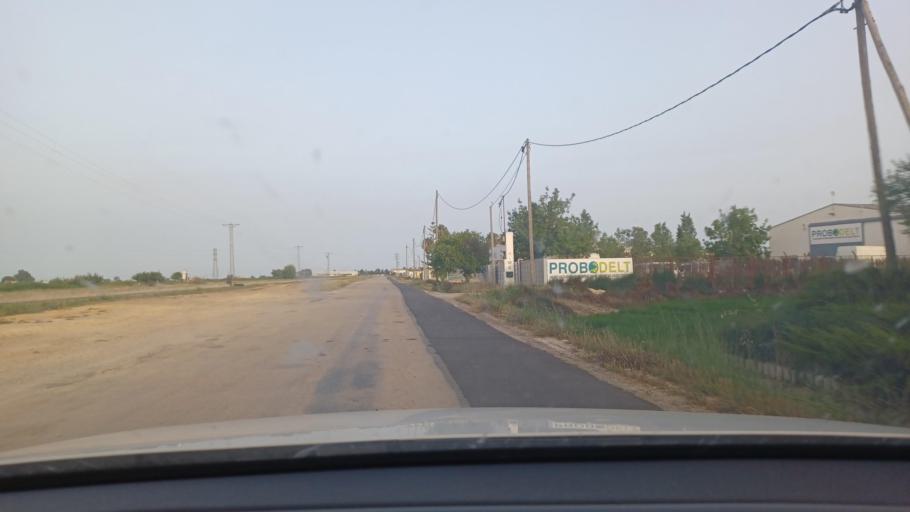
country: ES
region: Catalonia
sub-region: Provincia de Tarragona
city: Amposta
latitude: 40.7058
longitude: 0.5921
